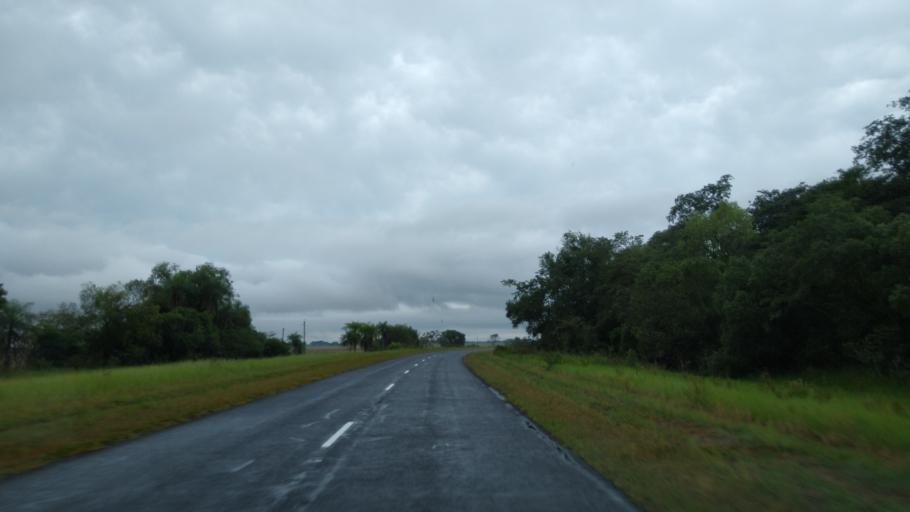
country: AR
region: Corrientes
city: Loreto
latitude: -27.7298
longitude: -57.2413
